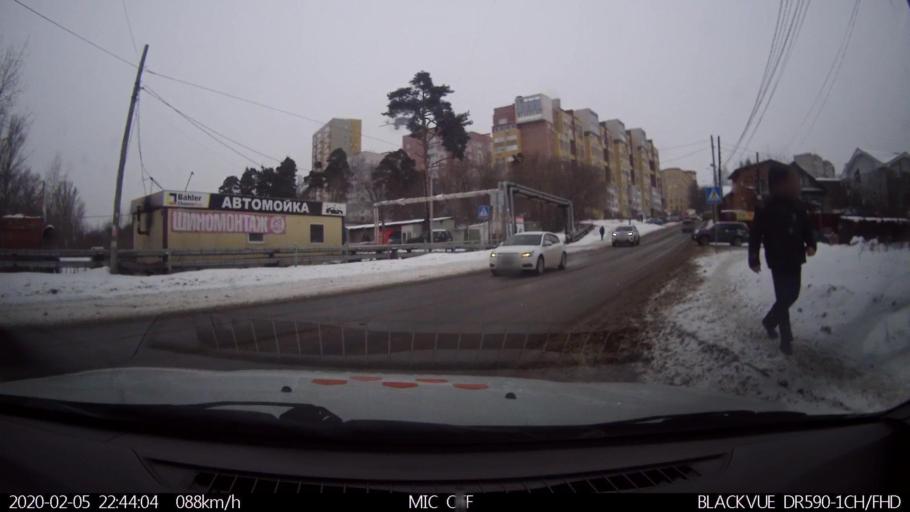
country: RU
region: Nizjnij Novgorod
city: Imeni Stepana Razina
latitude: 54.7097
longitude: 44.3970
